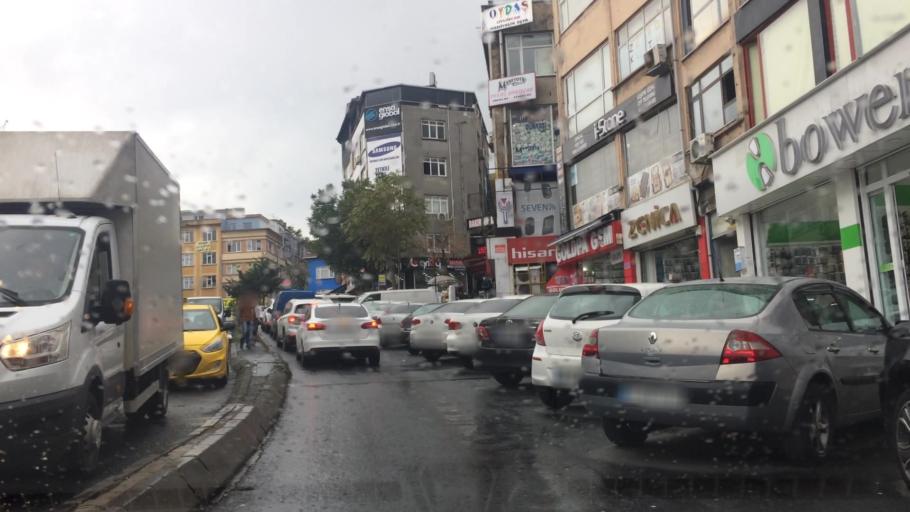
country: TR
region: Istanbul
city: Eminoenue
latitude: 41.0169
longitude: 28.9668
